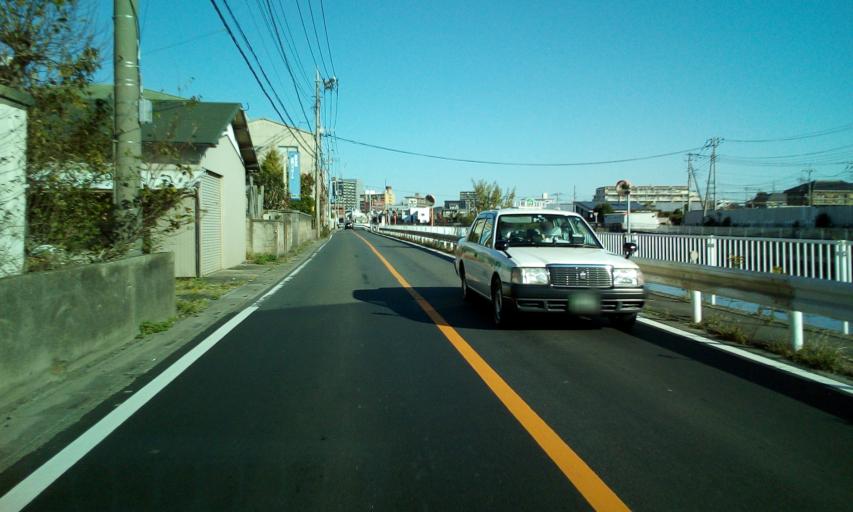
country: JP
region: Chiba
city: Nagareyama
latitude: 35.8368
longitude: 139.8839
